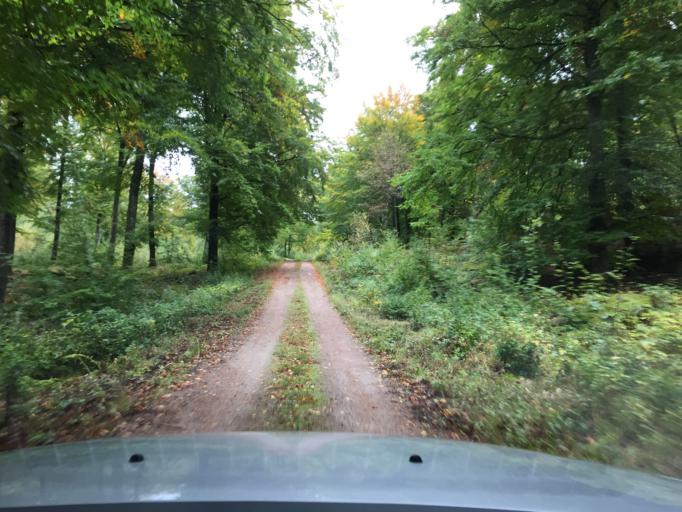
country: SE
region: Skane
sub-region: Hassleholms Kommun
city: Tormestorp
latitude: 56.0567
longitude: 13.7593
